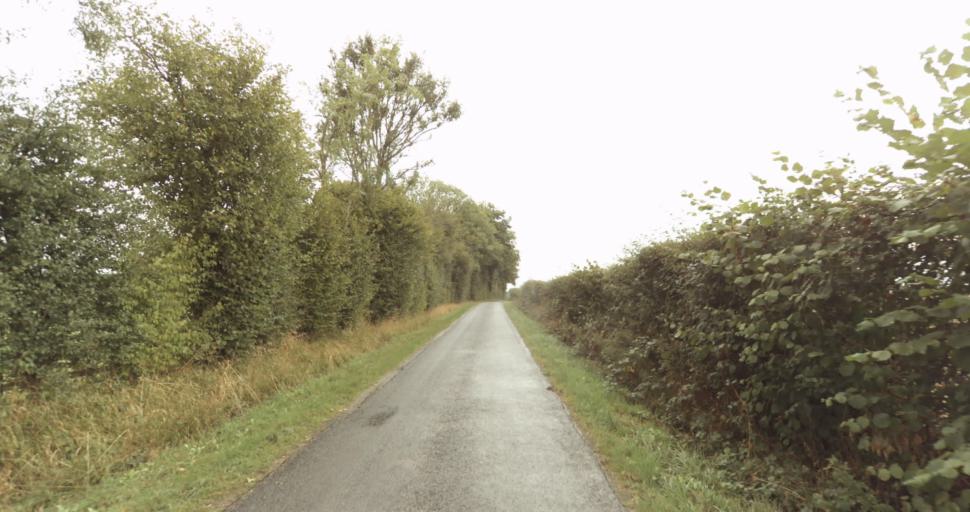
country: FR
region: Lower Normandy
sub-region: Departement de l'Orne
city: Sainte-Gauburge-Sainte-Colombe
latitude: 48.6890
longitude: 0.4365
